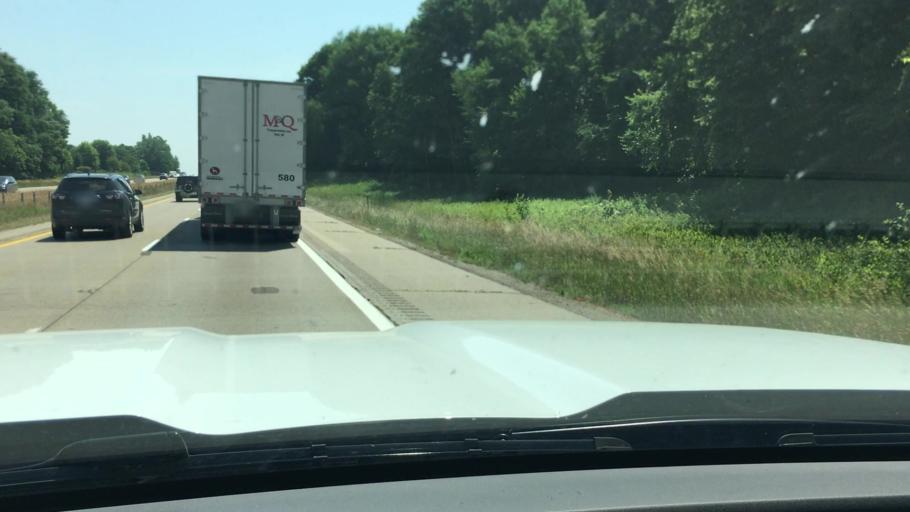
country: US
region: Michigan
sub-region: Ionia County
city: Portland
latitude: 42.8607
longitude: -84.8982
